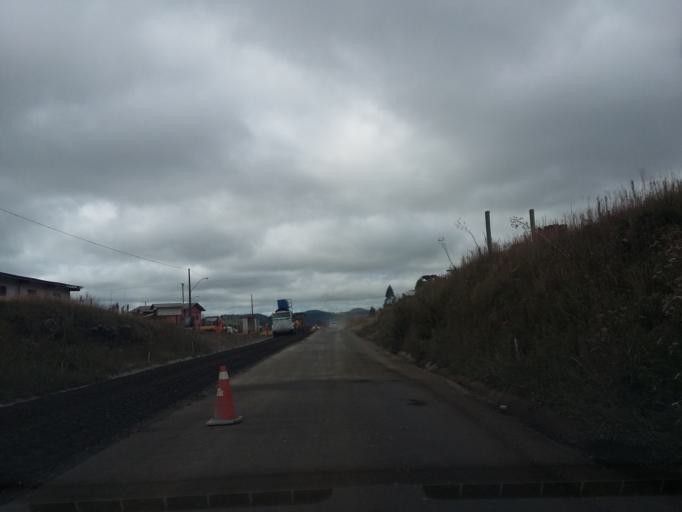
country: BR
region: Santa Catarina
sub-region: Lages
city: Lages
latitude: -27.9057
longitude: -50.1183
